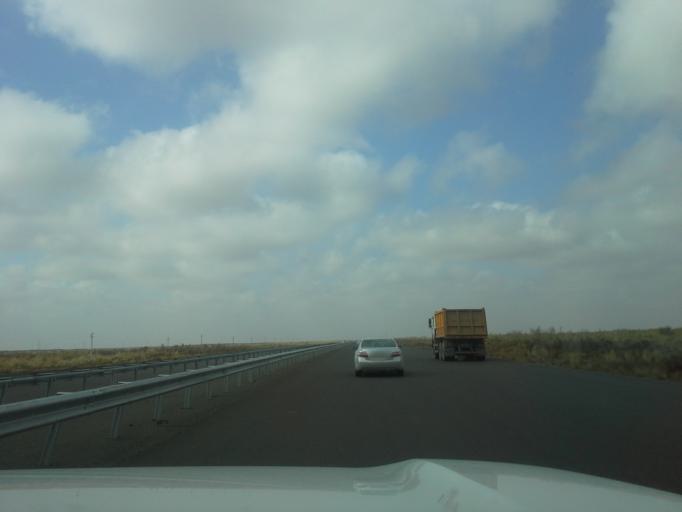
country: TM
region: Mary
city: Mary
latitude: 37.4243
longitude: 61.5862
